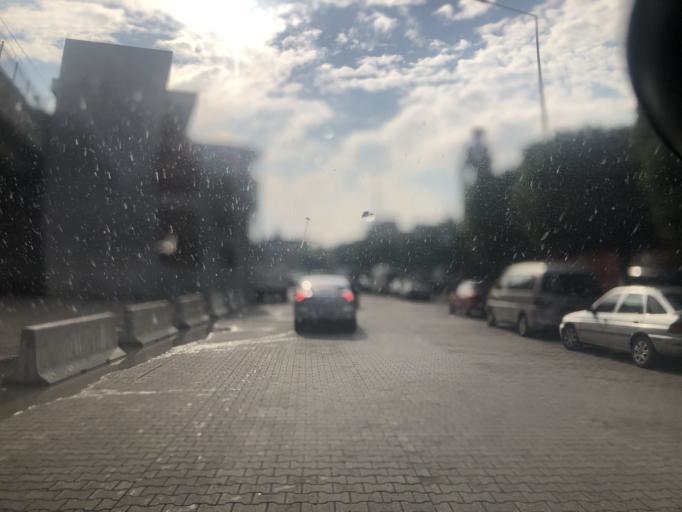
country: TR
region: Adana
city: Seyhan
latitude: 36.9853
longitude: 35.3189
